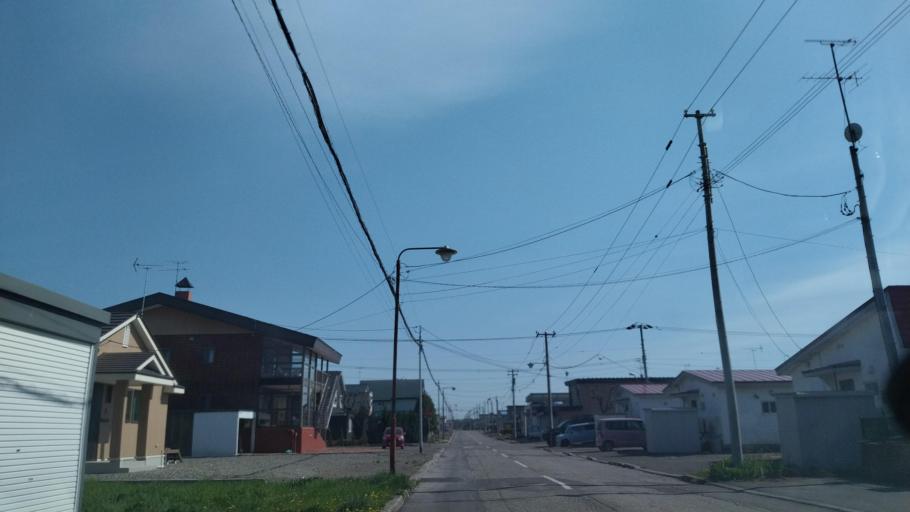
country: JP
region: Hokkaido
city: Obihiro
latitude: 42.9193
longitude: 143.0548
